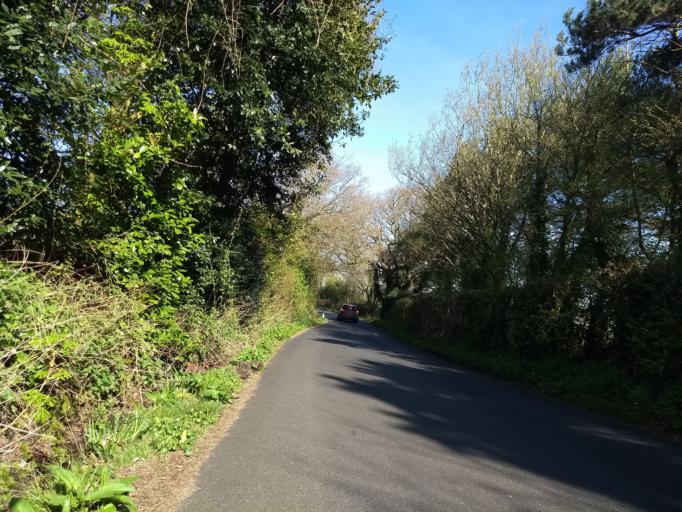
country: GB
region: England
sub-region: Isle of Wight
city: East Cowes
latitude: 50.7300
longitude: -1.2432
